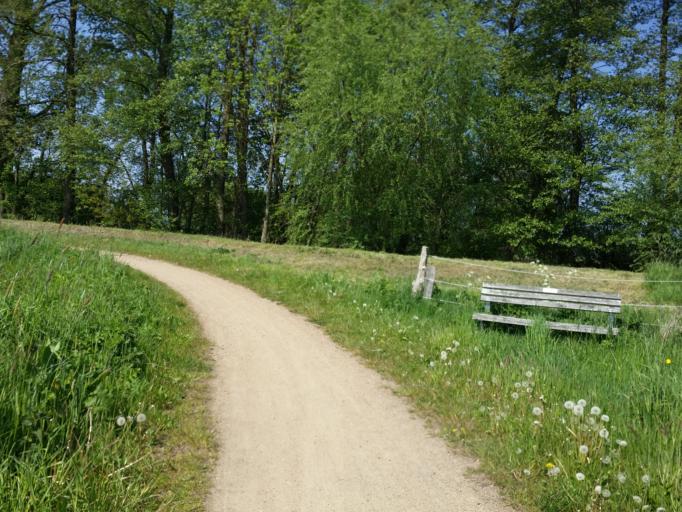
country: DE
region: Lower Saxony
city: Osterholz-Scharmbeck
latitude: 53.2154
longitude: 8.8612
